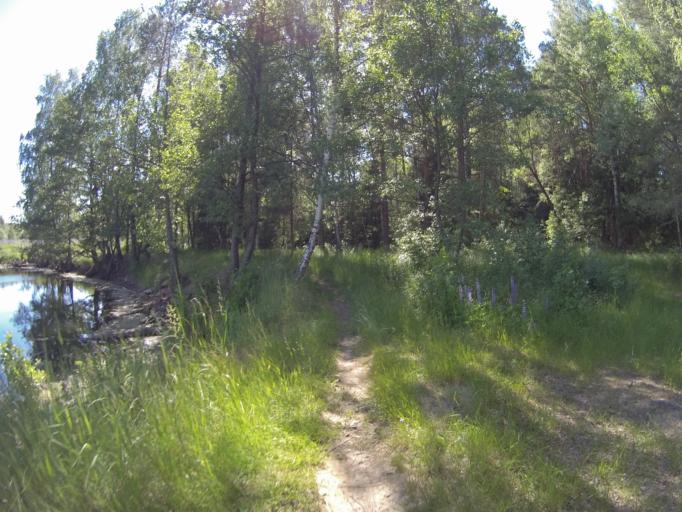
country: RU
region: Vladimir
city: Golovino
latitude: 55.9801
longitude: 40.3931
